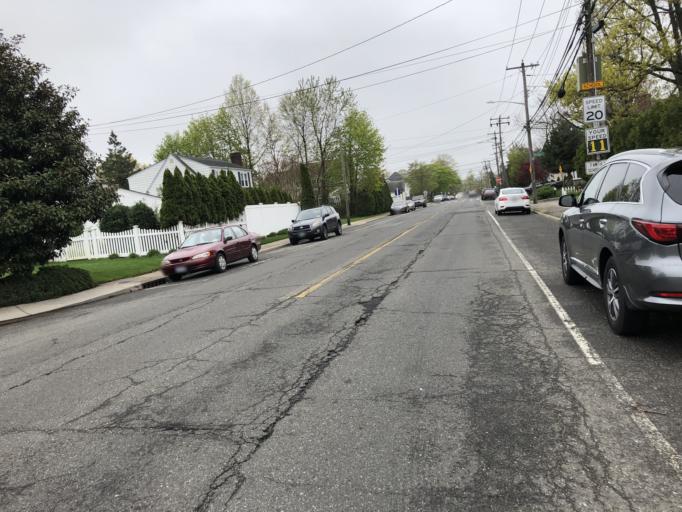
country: US
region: New York
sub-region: Nassau County
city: Hewlett Harbor
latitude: 40.6459
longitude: -73.6799
